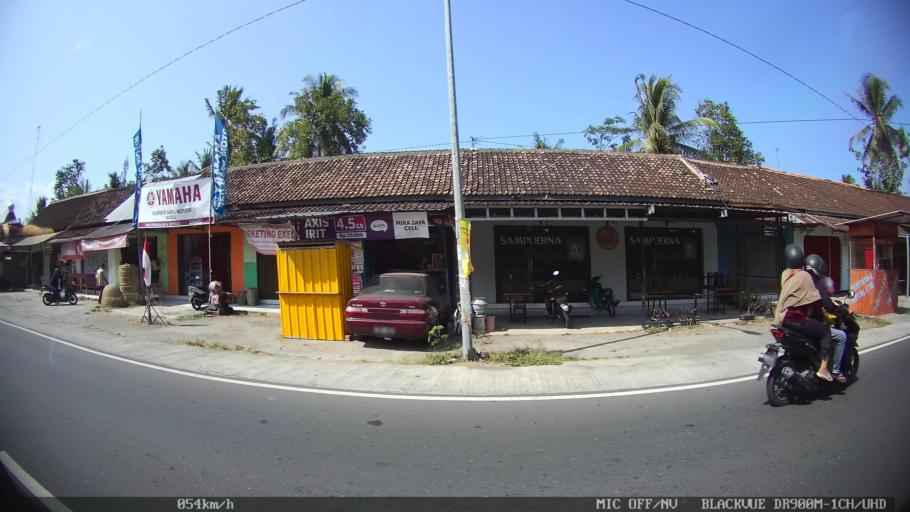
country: ID
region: Daerah Istimewa Yogyakarta
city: Srandakan
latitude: -7.9297
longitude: 110.2002
